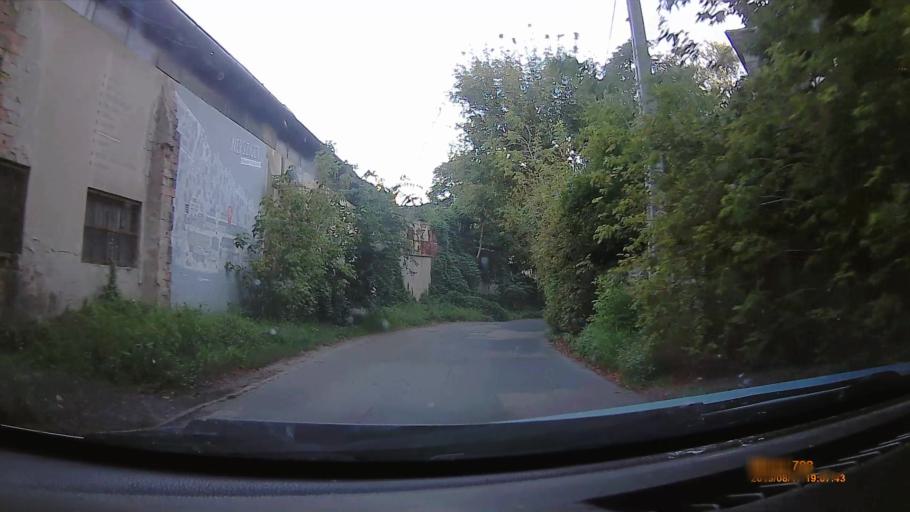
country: HU
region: Budapest
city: Budapest IV. keruelet
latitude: 47.5661
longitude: 19.0753
